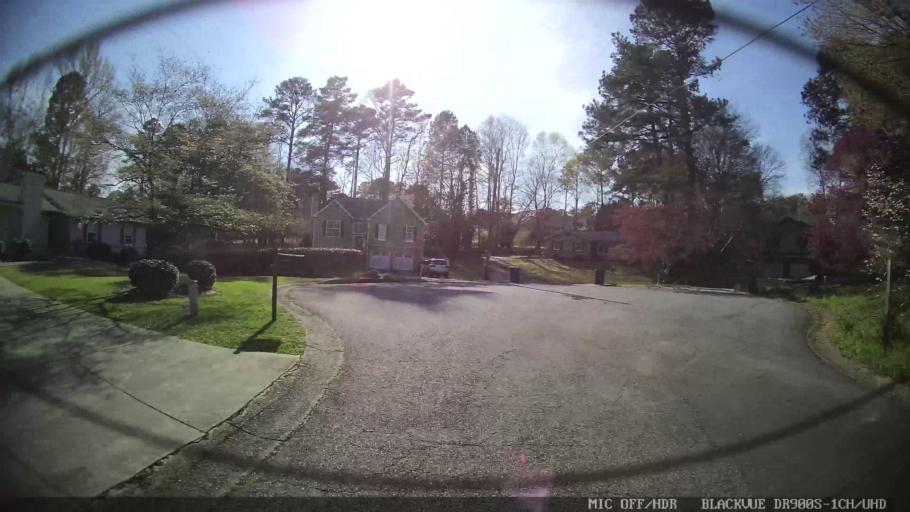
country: US
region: Georgia
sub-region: Cobb County
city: Marietta
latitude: 33.9773
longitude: -84.4890
